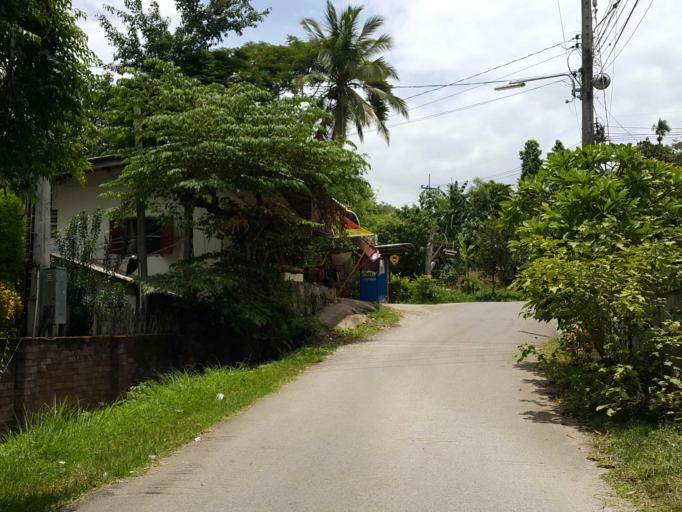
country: TH
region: Chiang Mai
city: Hang Dong
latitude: 18.7641
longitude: 98.8716
